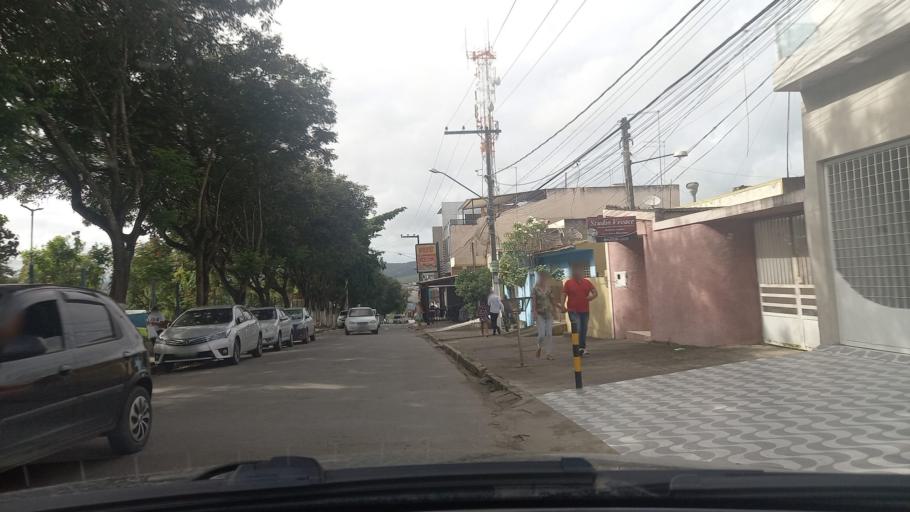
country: BR
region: Pernambuco
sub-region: Vitoria De Santo Antao
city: Vitoria de Santo Antao
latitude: -8.1086
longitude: -35.2997
